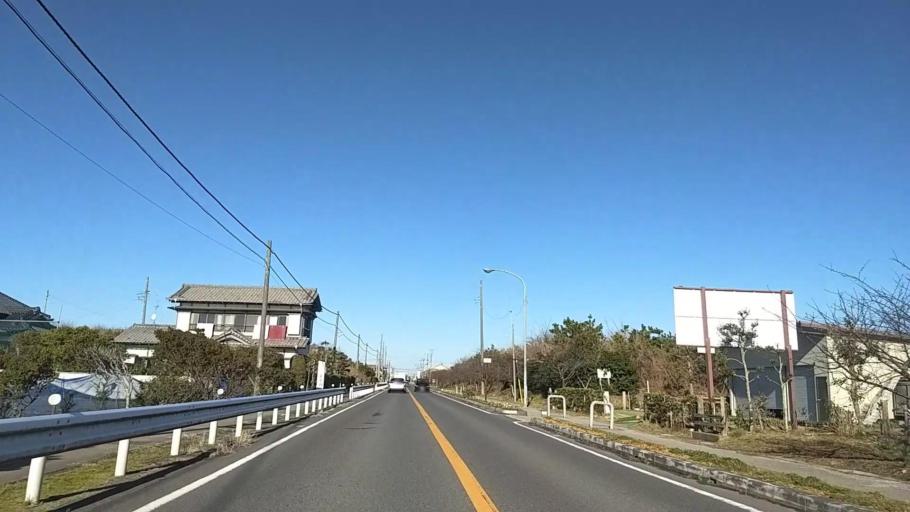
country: JP
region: Chiba
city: Togane
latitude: 35.4687
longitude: 140.4113
